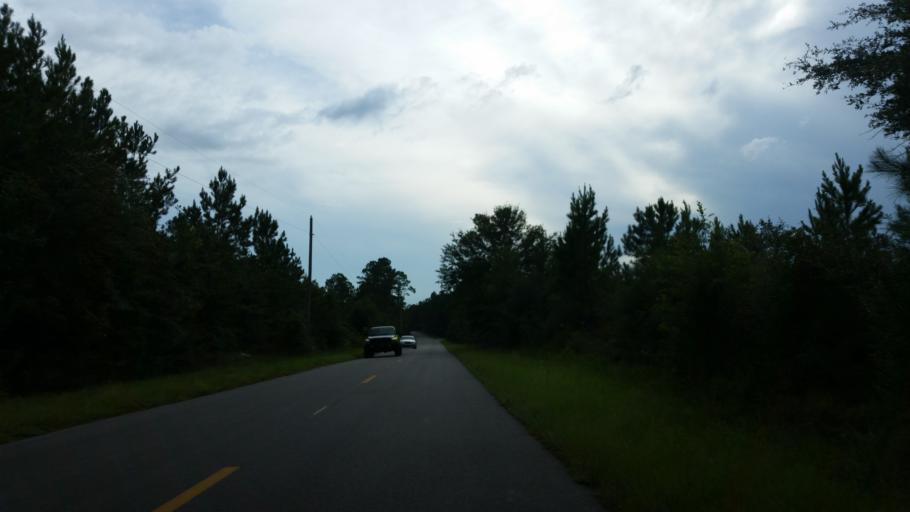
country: US
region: Florida
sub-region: Santa Rosa County
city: Point Baker
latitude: 30.7090
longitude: -86.9332
